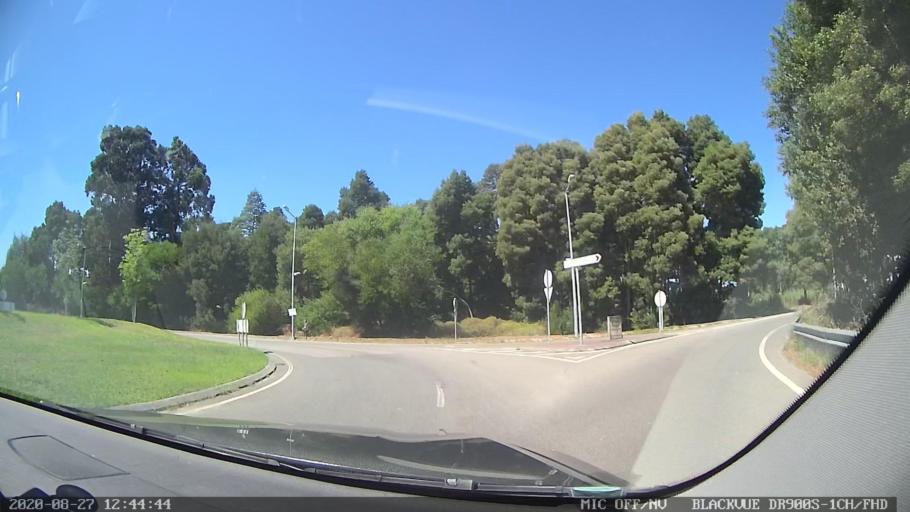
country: PT
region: Aveiro
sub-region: Ilhavo
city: Ilhavo
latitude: 40.6233
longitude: -8.6860
